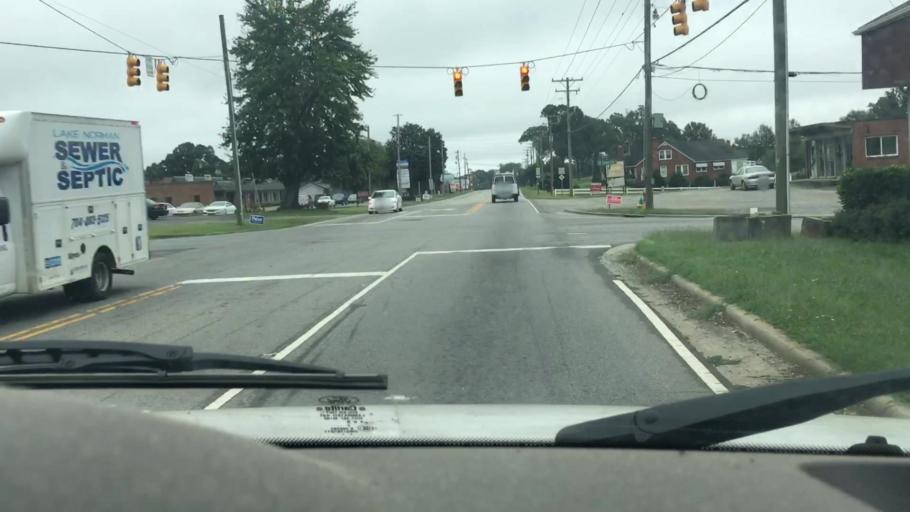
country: US
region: North Carolina
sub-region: Lincoln County
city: Denver
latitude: 35.5314
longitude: -81.0291
